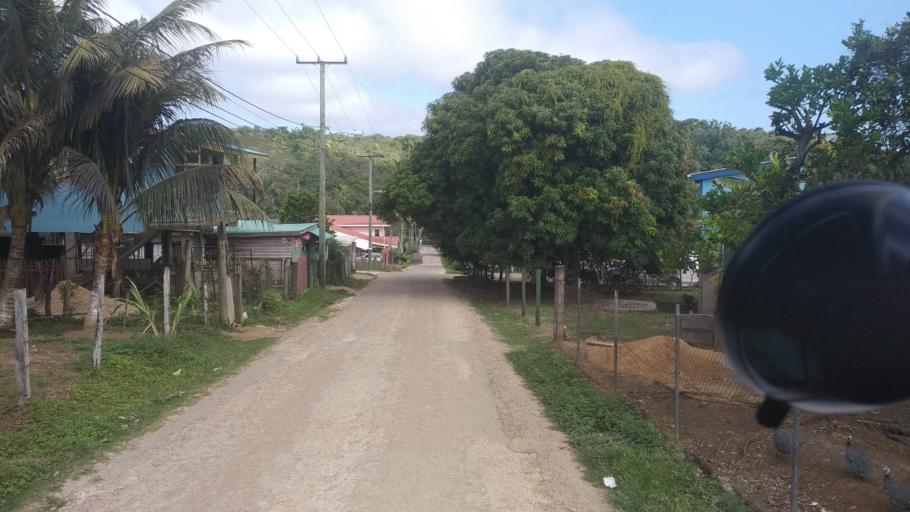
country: BZ
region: Cayo
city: Benque Viejo del Carmen
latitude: 17.0841
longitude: -89.1307
